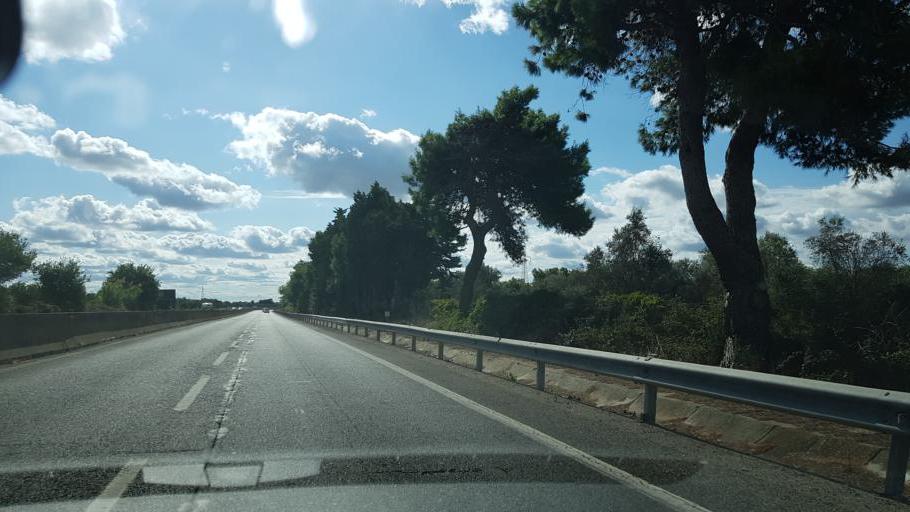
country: IT
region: Apulia
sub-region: Provincia di Brindisi
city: San Pietro Vernotico
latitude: 40.5171
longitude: 18.0199
